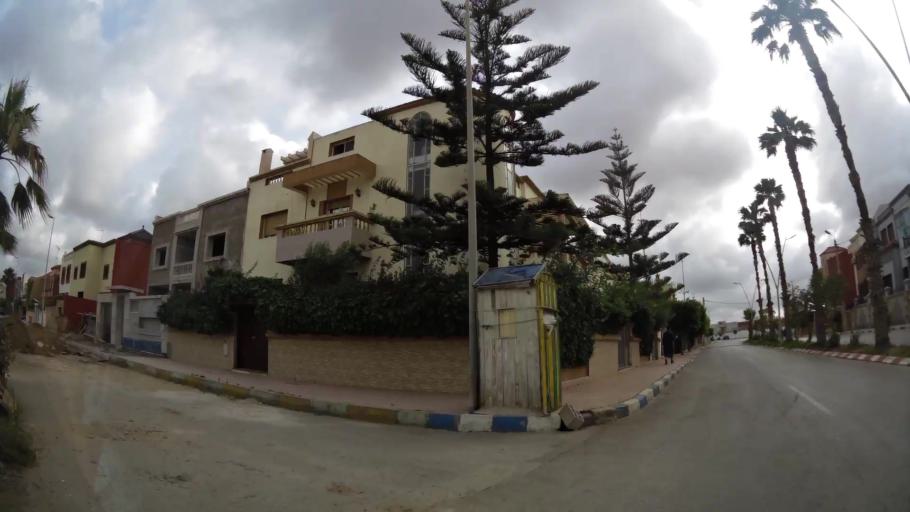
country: MA
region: Oriental
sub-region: Nador
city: Nador
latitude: 35.1665
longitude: -2.9147
